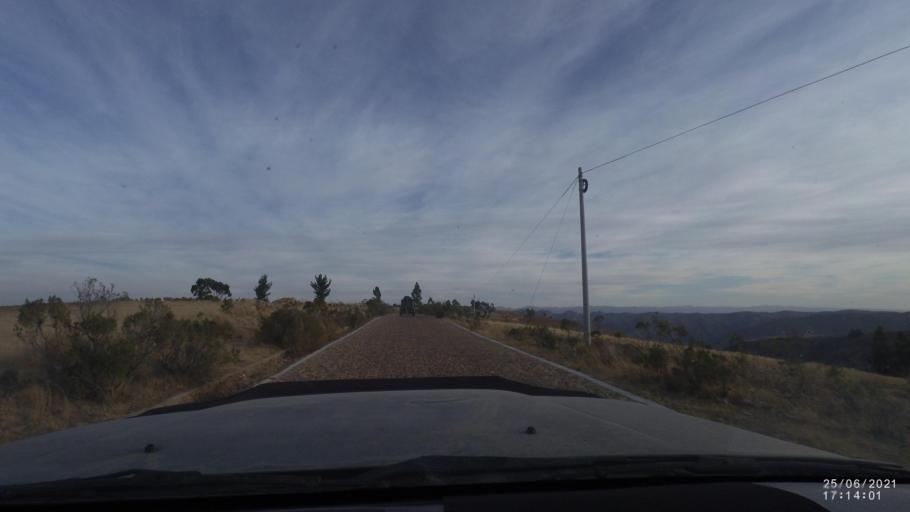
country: BO
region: Cochabamba
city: Arani
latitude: -17.8632
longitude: -65.6961
